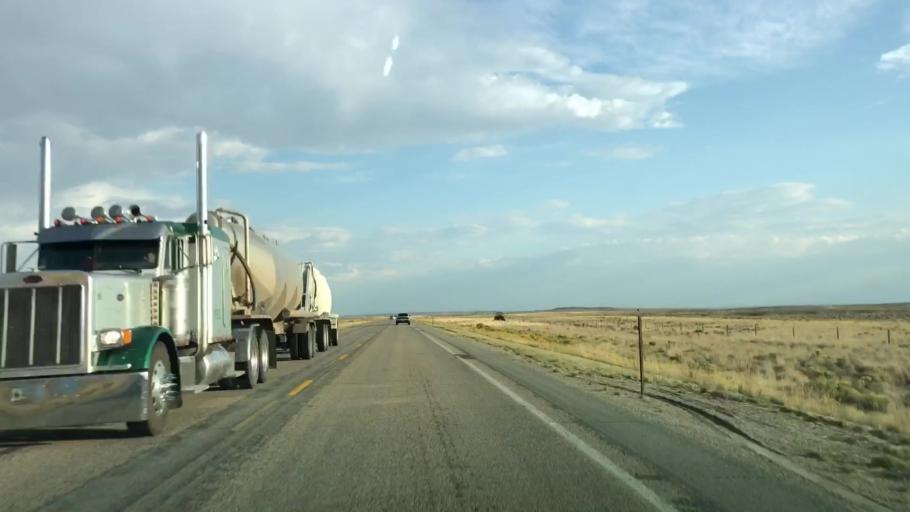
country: US
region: Wyoming
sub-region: Sublette County
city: Pinedale
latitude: 42.4028
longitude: -109.5477
